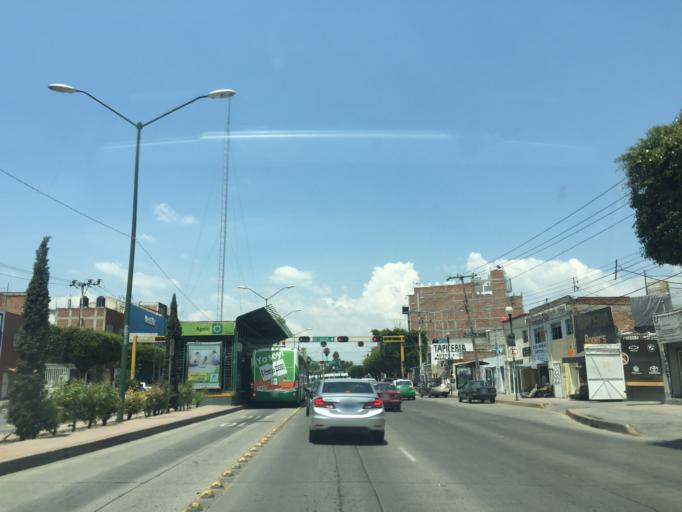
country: MX
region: Guanajuato
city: Leon
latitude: 21.1288
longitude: -101.6873
